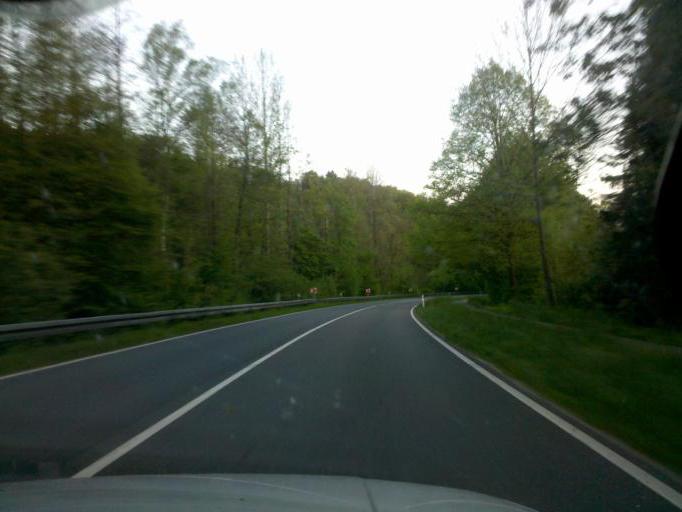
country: DE
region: North Rhine-Westphalia
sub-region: Regierungsbezirk Koln
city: Gummersbach
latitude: 51.0051
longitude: 7.5582
